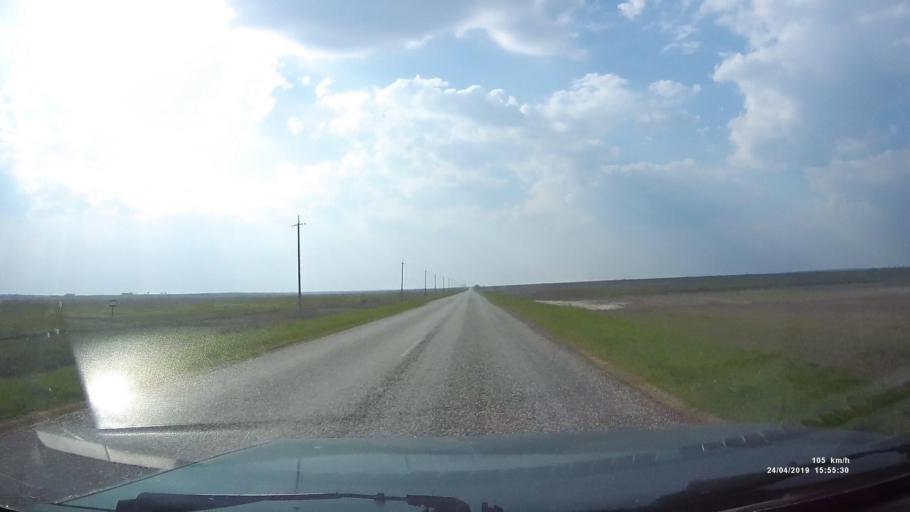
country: RU
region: Kalmykiya
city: Yashalta
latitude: 46.5909
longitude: 42.5481
